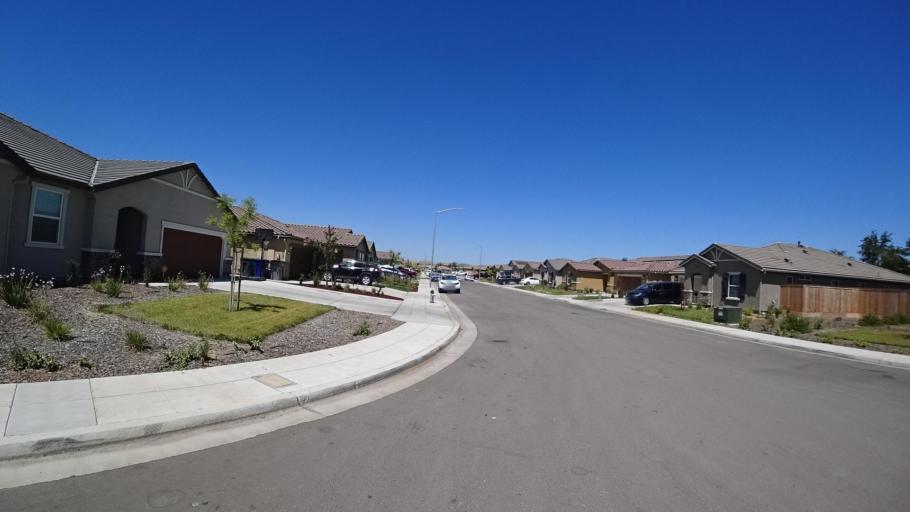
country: US
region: California
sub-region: Fresno County
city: Sunnyside
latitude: 36.7253
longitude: -119.6652
